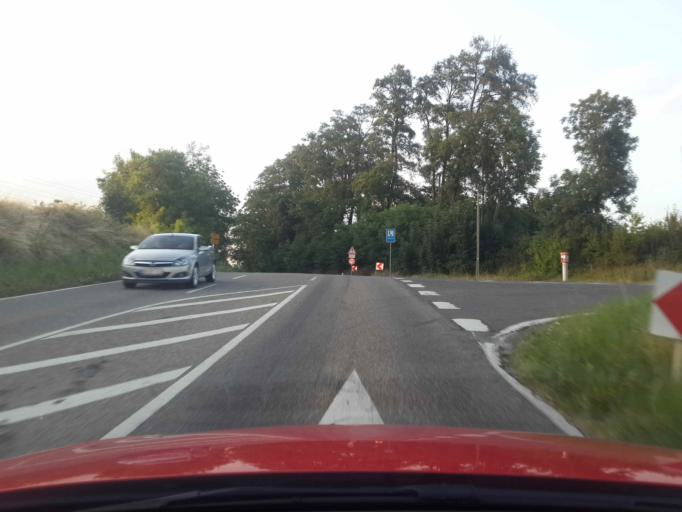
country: DE
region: Baden-Wuerttemberg
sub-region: Regierungsbezirk Stuttgart
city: Nordheim
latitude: 49.1244
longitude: 9.1305
